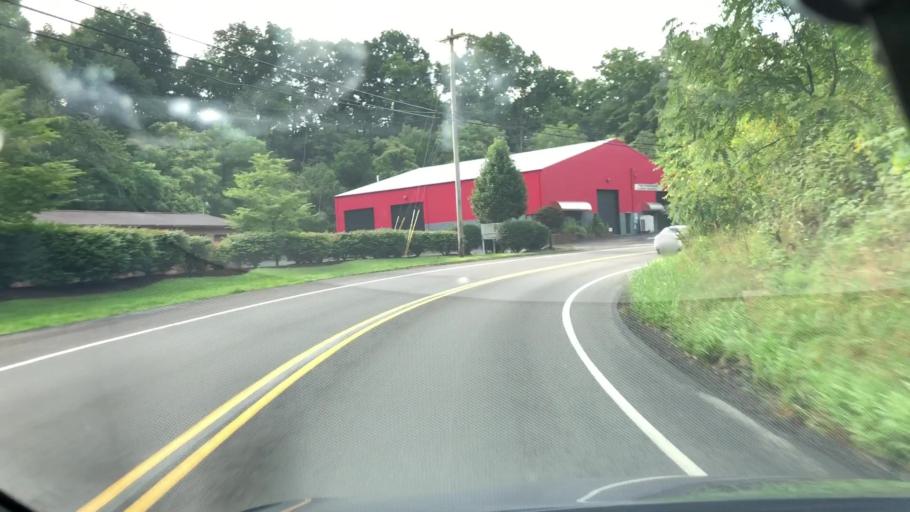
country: US
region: Pennsylvania
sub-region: Washington County
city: Thompsonville
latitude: 40.2931
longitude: -80.1061
